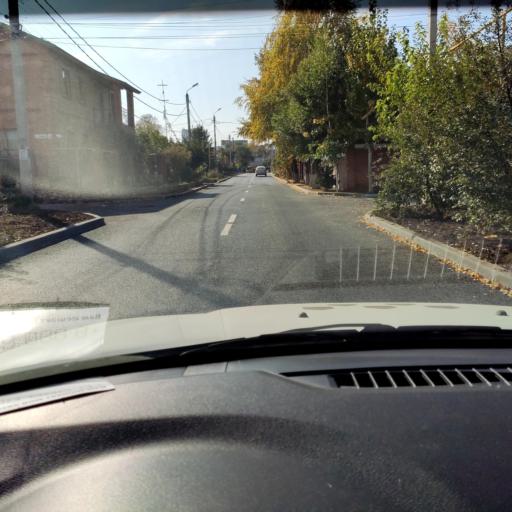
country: RU
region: Samara
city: Tol'yatti
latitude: 53.5269
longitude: 49.4166
